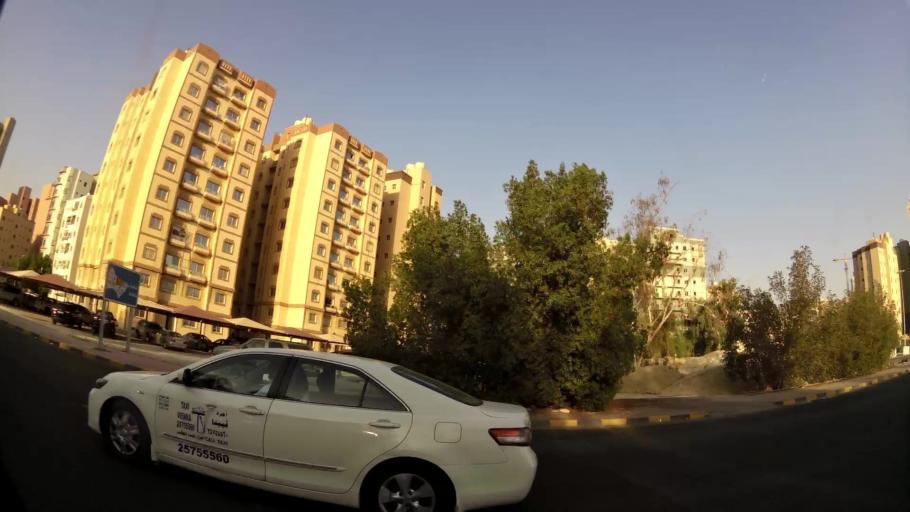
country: KW
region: Muhafazat Hawalli
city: As Salimiyah
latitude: 29.3364
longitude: 48.0713
